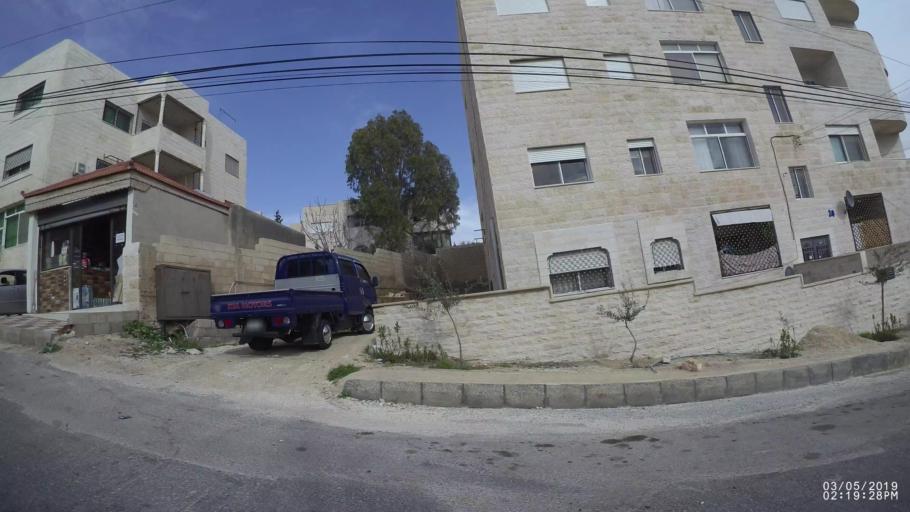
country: JO
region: Amman
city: Amman
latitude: 32.0087
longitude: 35.9351
